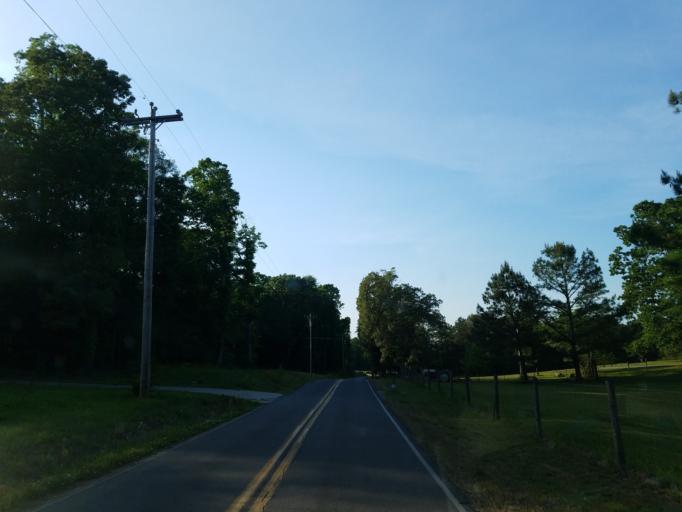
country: US
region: Georgia
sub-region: Gordon County
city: Calhoun
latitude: 34.4980
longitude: -85.1147
